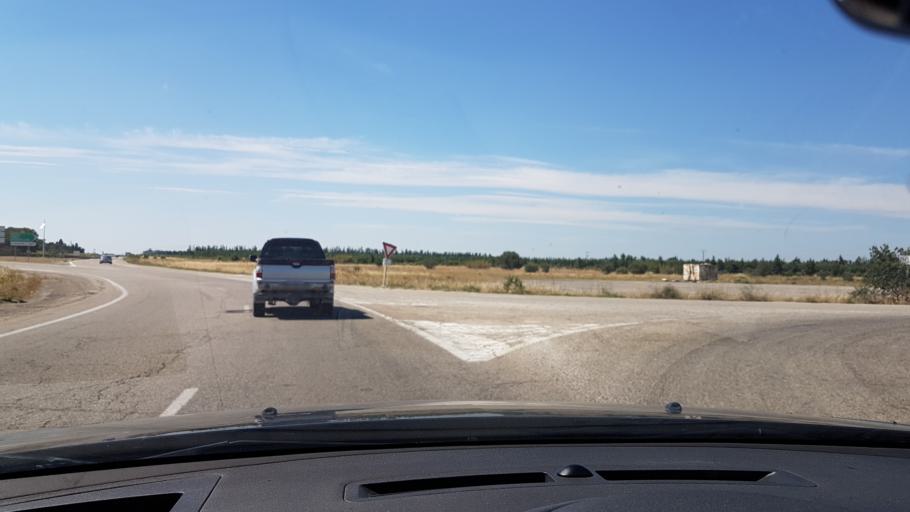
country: FR
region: Provence-Alpes-Cote d'Azur
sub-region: Departement des Bouches-du-Rhone
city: Fos-sur-Mer
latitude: 43.4868
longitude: 4.8866
